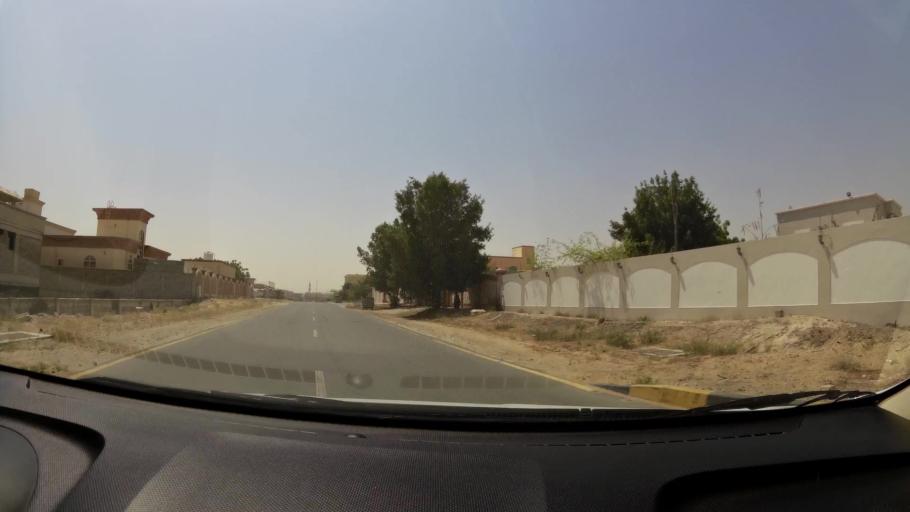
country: AE
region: Ajman
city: Ajman
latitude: 25.4206
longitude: 55.5273
